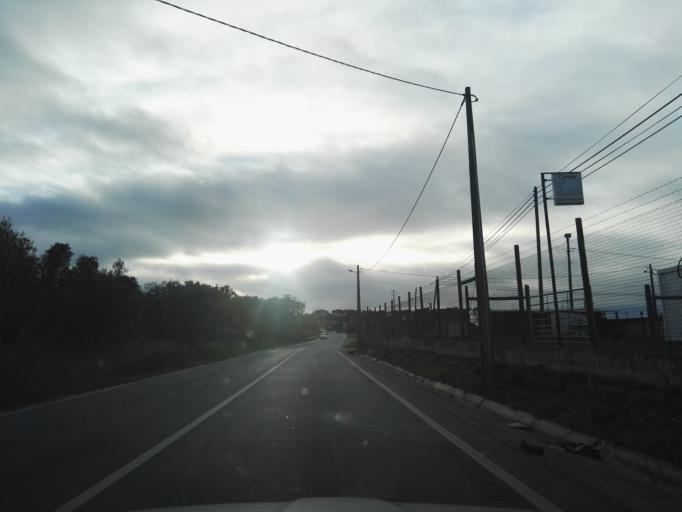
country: PT
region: Evora
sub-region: Evora
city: Evora
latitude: 38.5898
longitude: -7.8631
